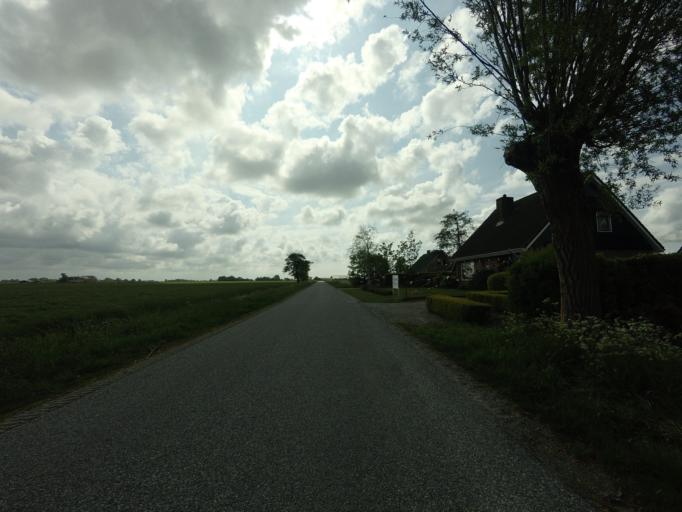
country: NL
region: Friesland
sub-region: Sudwest Fryslan
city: Sneek
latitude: 53.0576
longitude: 5.6211
